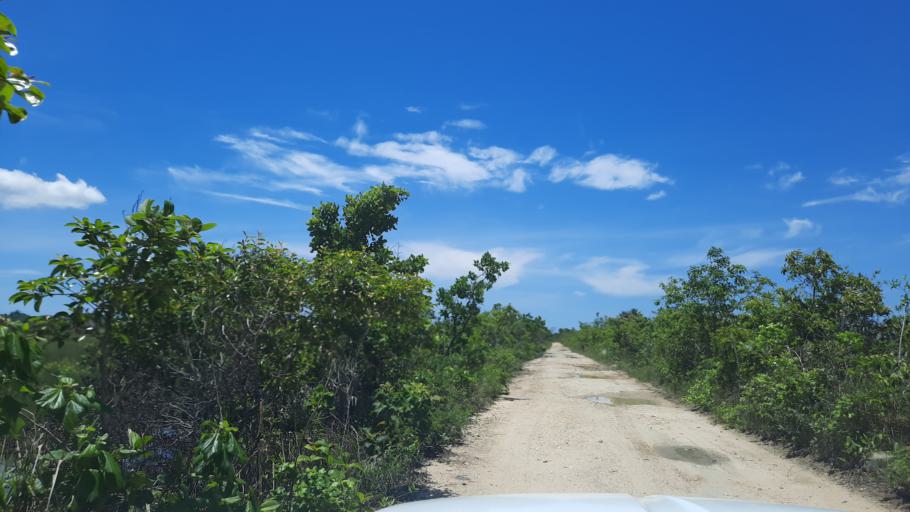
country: BZ
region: Cayo
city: Belmopan
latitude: 17.3808
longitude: -88.4915
